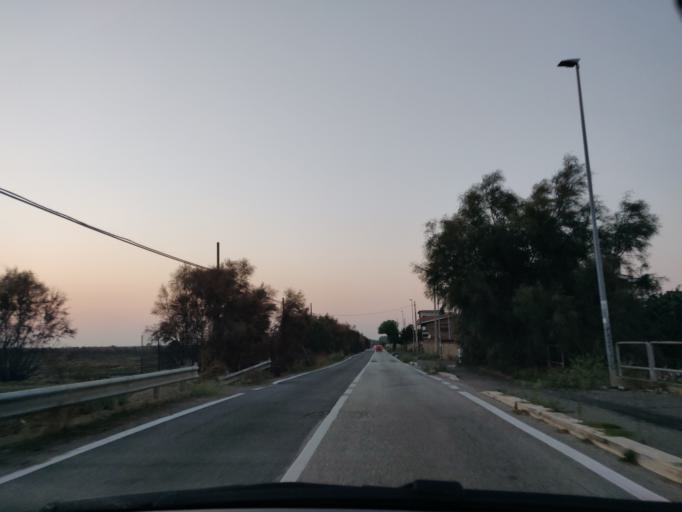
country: IT
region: Latium
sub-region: Citta metropolitana di Roma Capitale
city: Npp 23 (Parco Leonardo)
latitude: 41.8161
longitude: 12.2988
